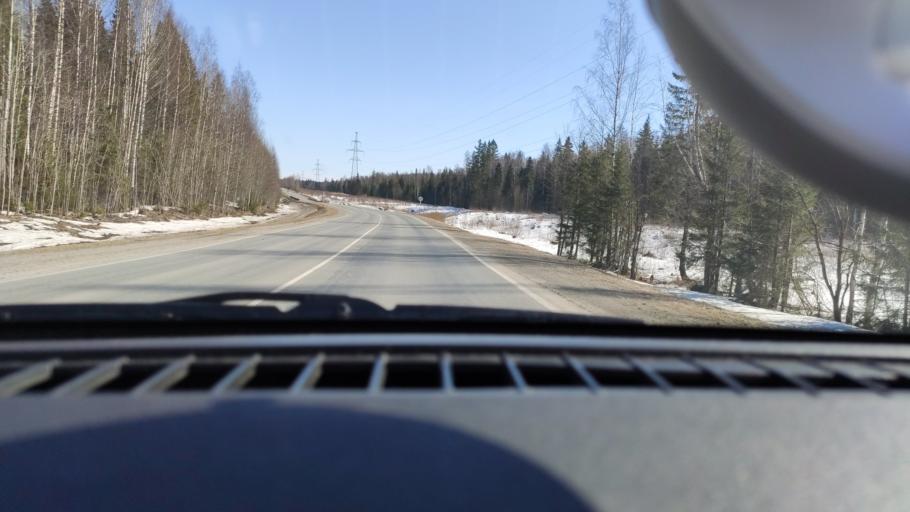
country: RU
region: Perm
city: Perm
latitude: 58.1386
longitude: 56.2736
